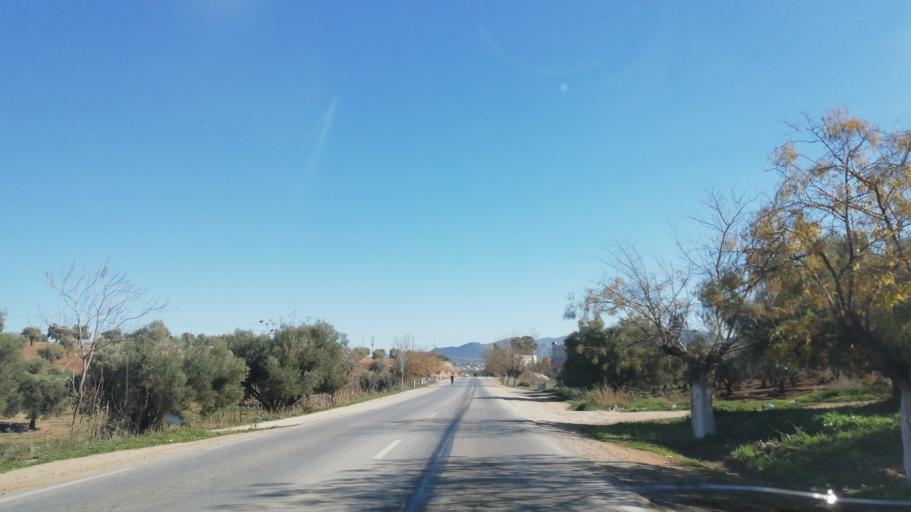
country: DZ
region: Tlemcen
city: Beni Mester
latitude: 34.8254
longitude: -1.5579
